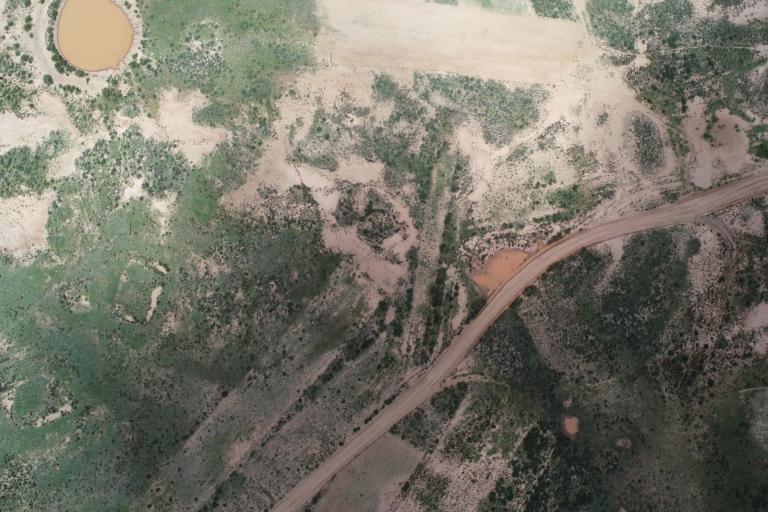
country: BO
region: La Paz
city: Curahuara de Carangas
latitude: -17.3239
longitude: -68.5002
